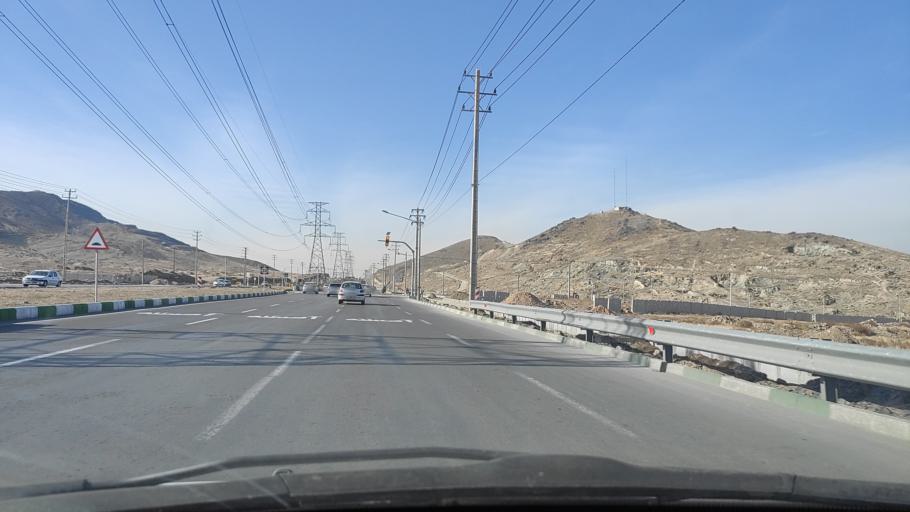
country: IR
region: Razavi Khorasan
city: Mashhad
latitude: 36.2808
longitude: 59.5308
